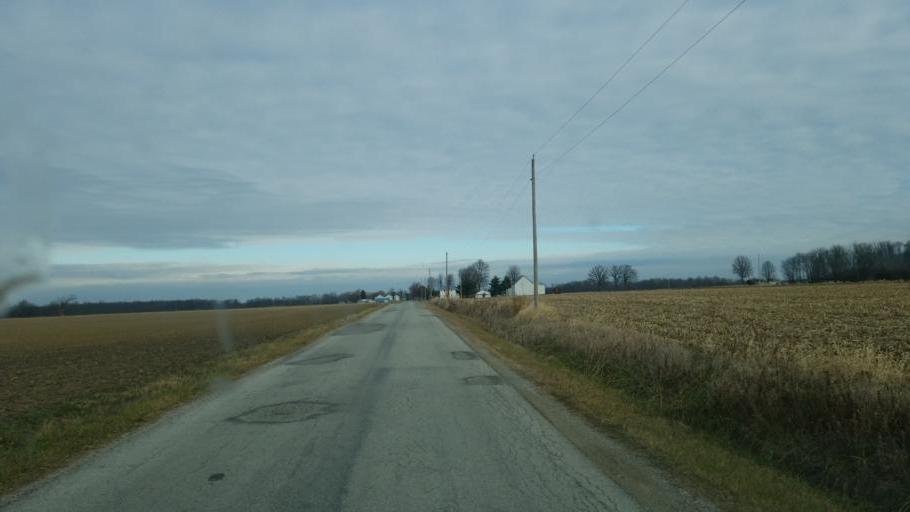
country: US
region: Ohio
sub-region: Morrow County
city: Mount Gilead
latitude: 40.6259
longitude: -82.9182
